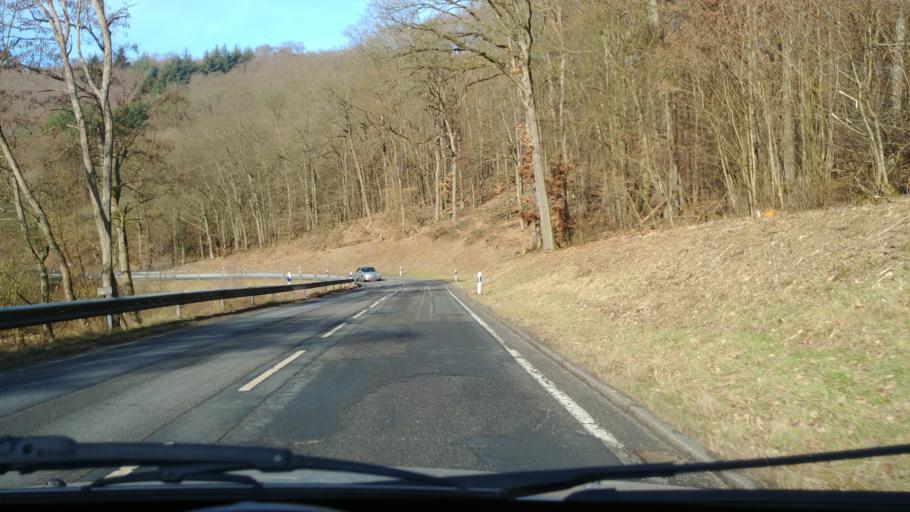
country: DE
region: Rheinland-Pfalz
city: Dachsenhausen
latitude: 50.2603
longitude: 7.6913
